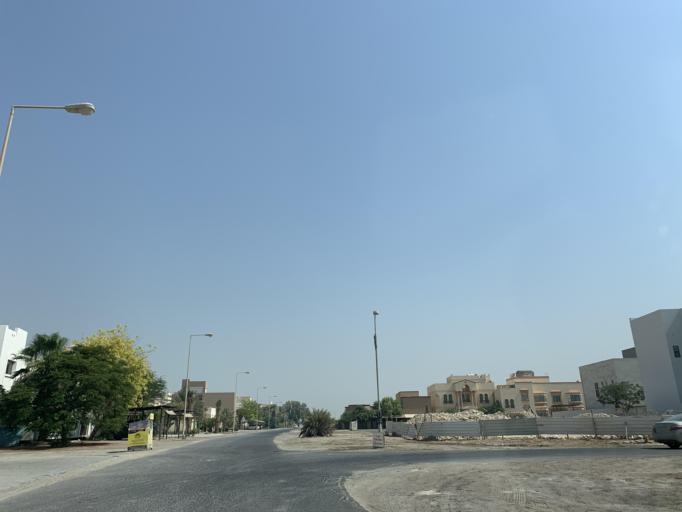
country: BH
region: Manama
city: Jidd Hafs
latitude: 26.1964
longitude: 50.5135
